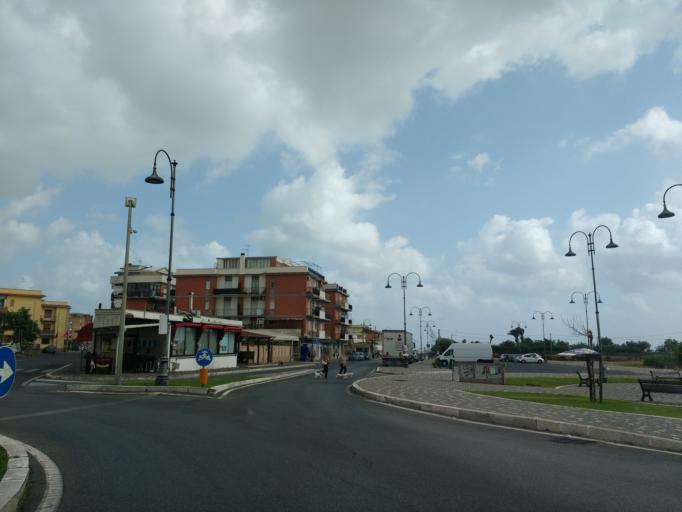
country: IT
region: Latium
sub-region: Citta metropolitana di Roma Capitale
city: Anzio
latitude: 41.4659
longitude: 12.6109
